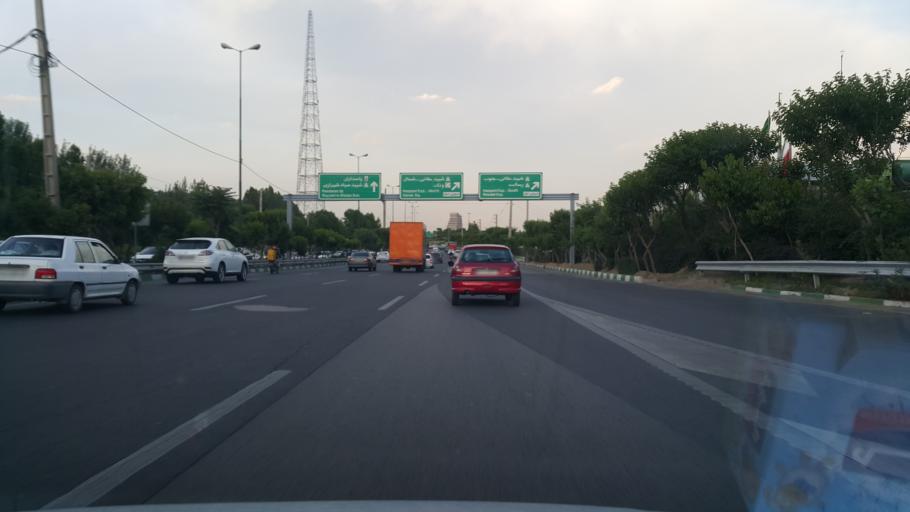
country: IR
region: Tehran
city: Tajrish
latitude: 35.7491
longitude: 51.4317
